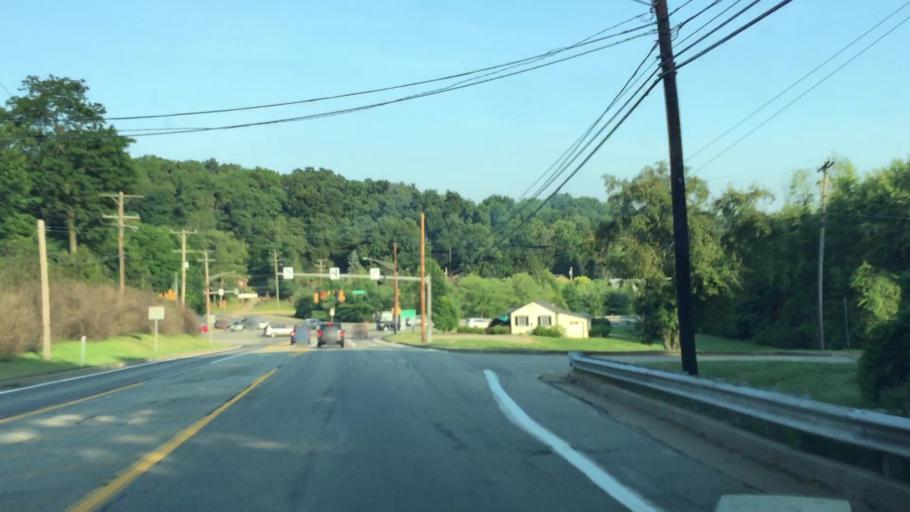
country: US
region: Pennsylvania
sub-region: Allegheny County
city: Bryn Mawr
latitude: 40.3146
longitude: -80.0912
